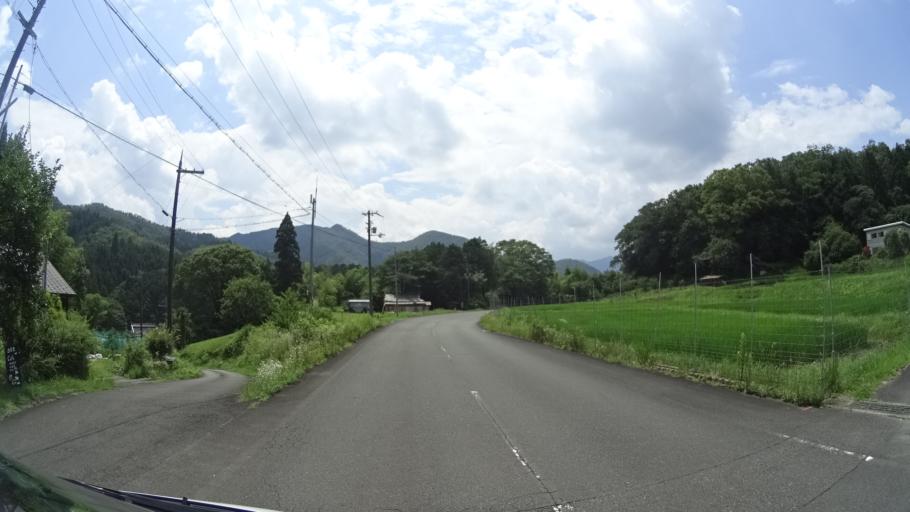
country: JP
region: Kyoto
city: Ayabe
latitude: 35.1794
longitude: 135.2795
